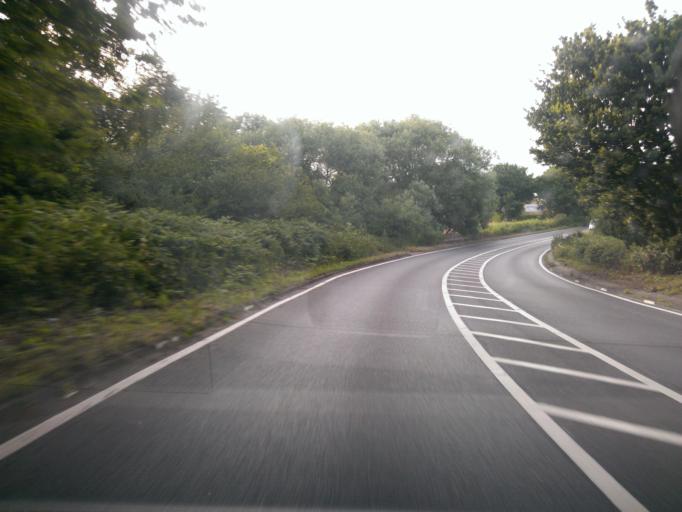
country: GB
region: England
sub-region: Essex
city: Alresford
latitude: 51.8697
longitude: 1.0140
